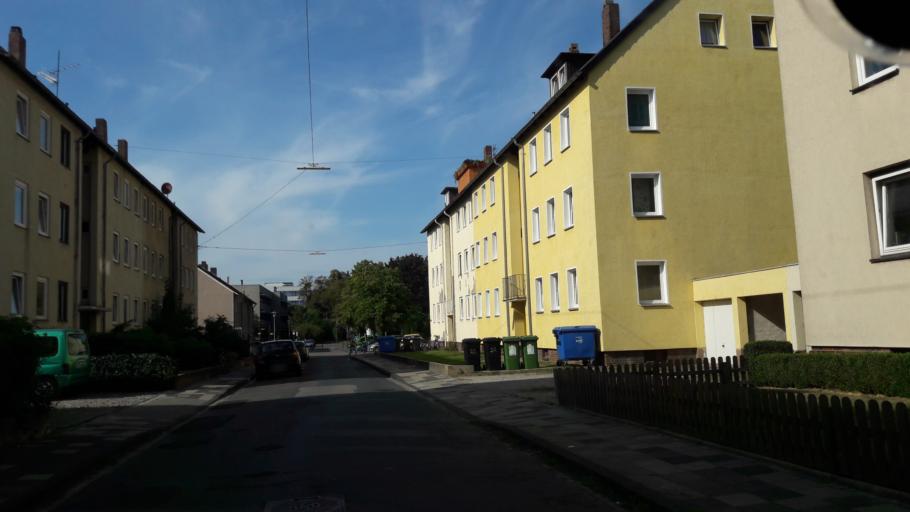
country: DE
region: Lower Saxony
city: Hildesheim
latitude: 52.1658
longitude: 9.9495
